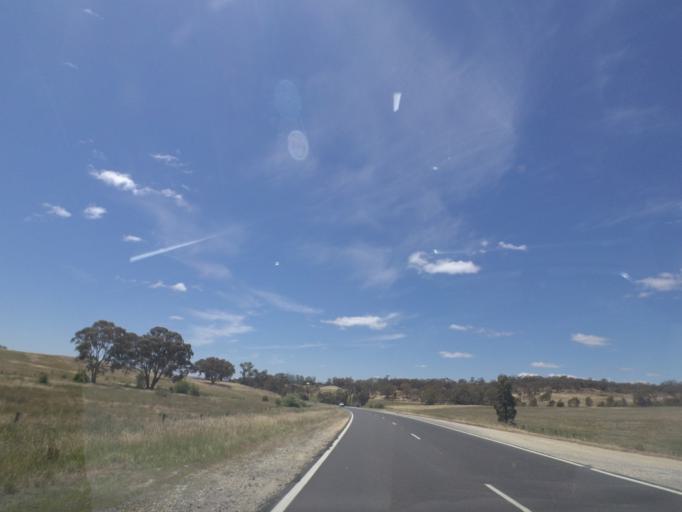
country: AU
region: Victoria
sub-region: Mount Alexander
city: Castlemaine
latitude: -37.1617
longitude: 144.1566
